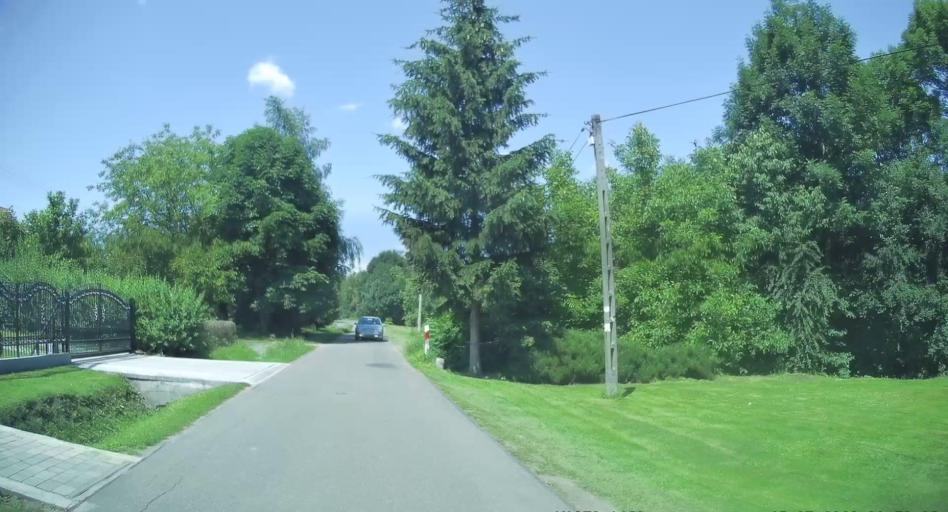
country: PL
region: Subcarpathian Voivodeship
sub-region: Powiat jaroslawski
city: Sosnica
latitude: 49.8642
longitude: 22.8748
